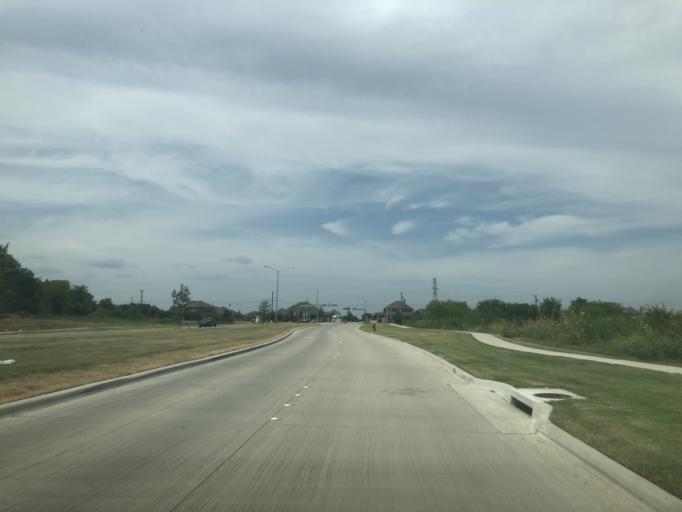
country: US
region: Texas
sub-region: Tarrant County
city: Saginaw
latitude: 32.8818
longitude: -97.3550
